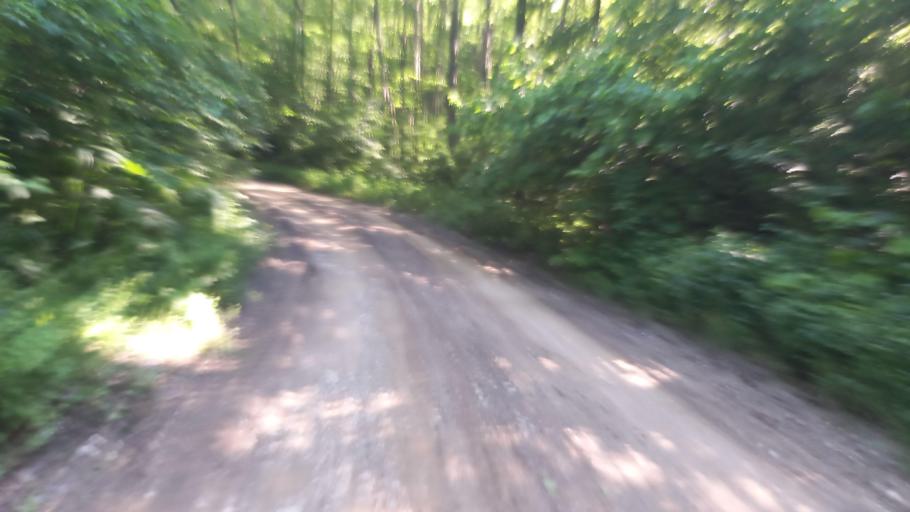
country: RU
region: Krasnodarskiy
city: Dzhubga
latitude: 44.5385
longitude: 38.7556
